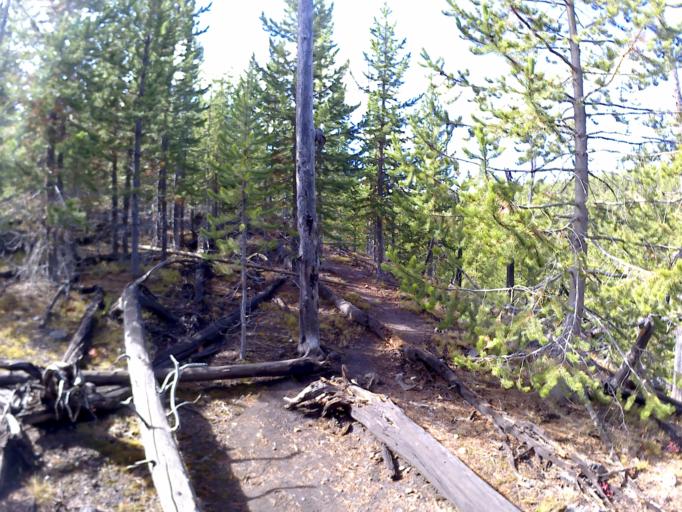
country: US
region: Montana
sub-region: Gallatin County
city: West Yellowstone
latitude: 44.4888
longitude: -110.8668
